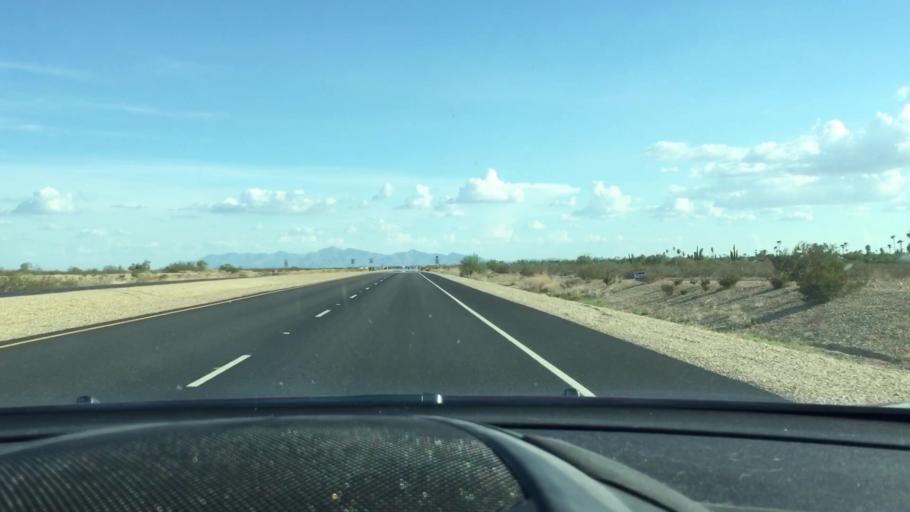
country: US
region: Arizona
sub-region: Maricopa County
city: Sun City West
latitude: 33.6788
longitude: -112.3231
